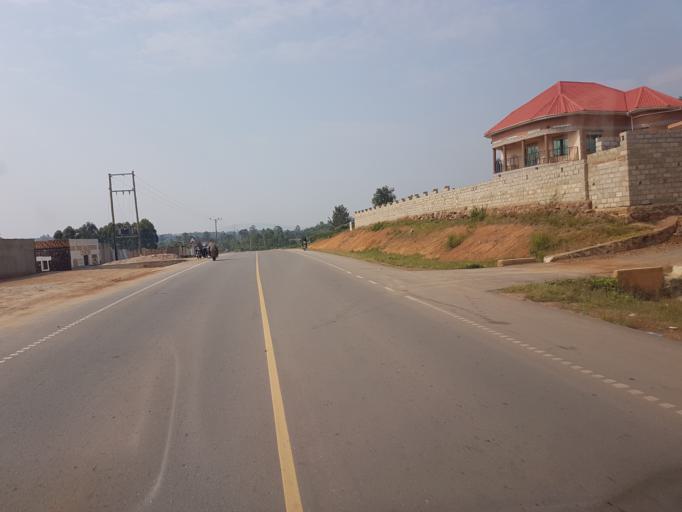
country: UG
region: Western Region
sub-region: Mbarara District
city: Bwizibwera
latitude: -0.6353
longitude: 30.6024
